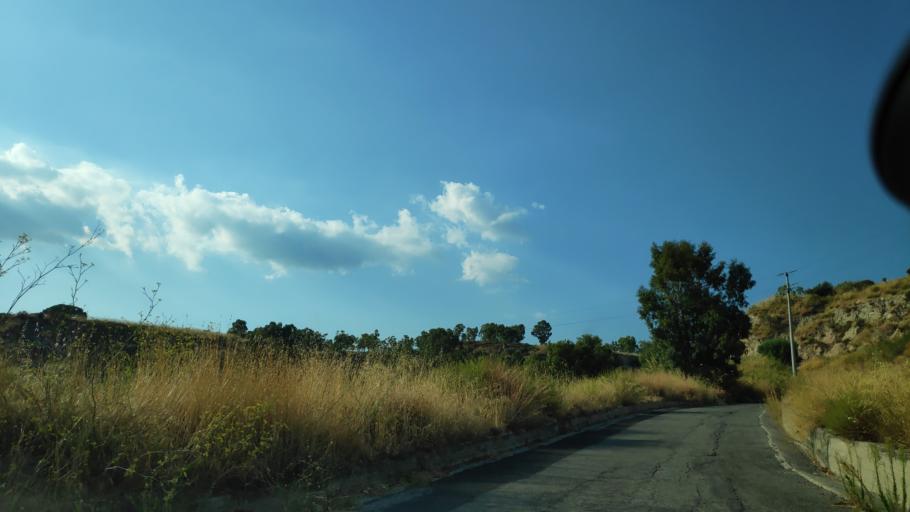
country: IT
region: Calabria
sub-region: Provincia di Catanzaro
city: Guardavalle
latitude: 38.5079
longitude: 16.5024
